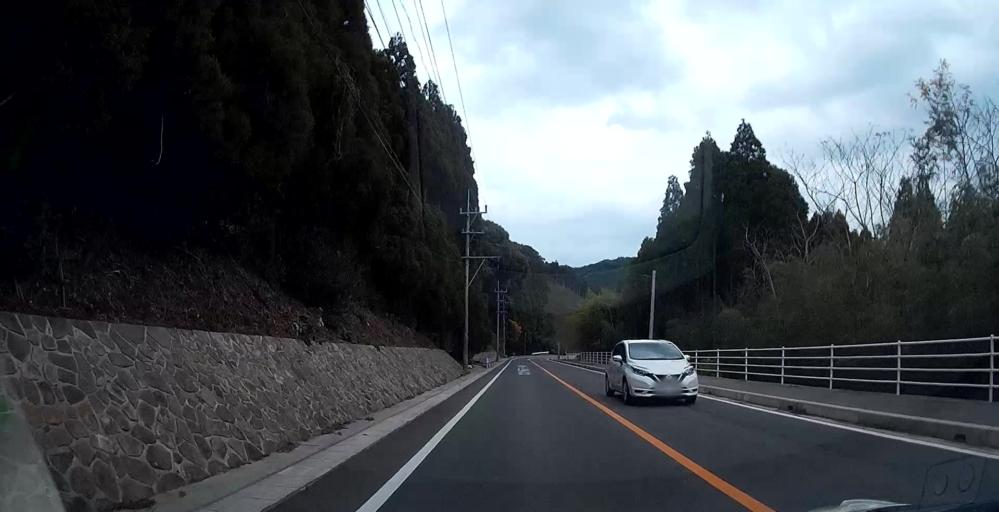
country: JP
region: Kagoshima
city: Akune
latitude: 32.0996
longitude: 130.1567
